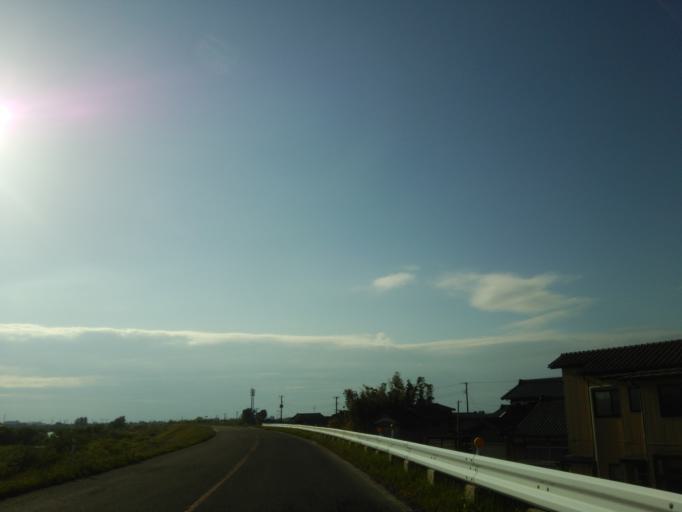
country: JP
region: Niigata
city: Gosen
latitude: 37.7813
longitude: 139.1937
